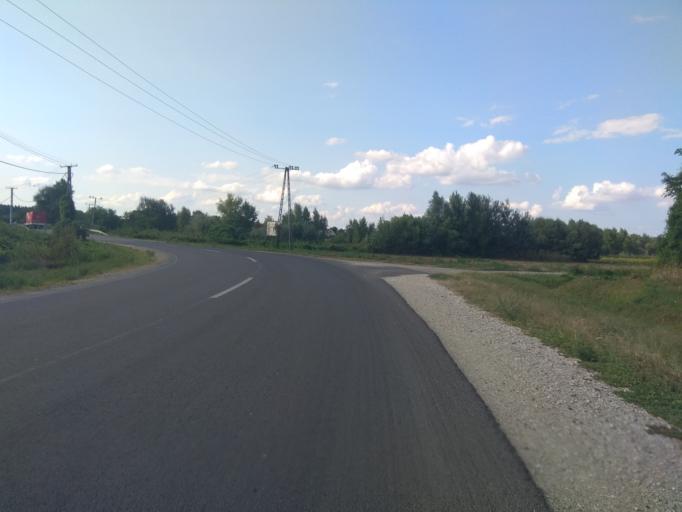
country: HU
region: Borsod-Abauj-Zemplen
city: Mezocsat
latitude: 47.8385
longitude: 20.9004
